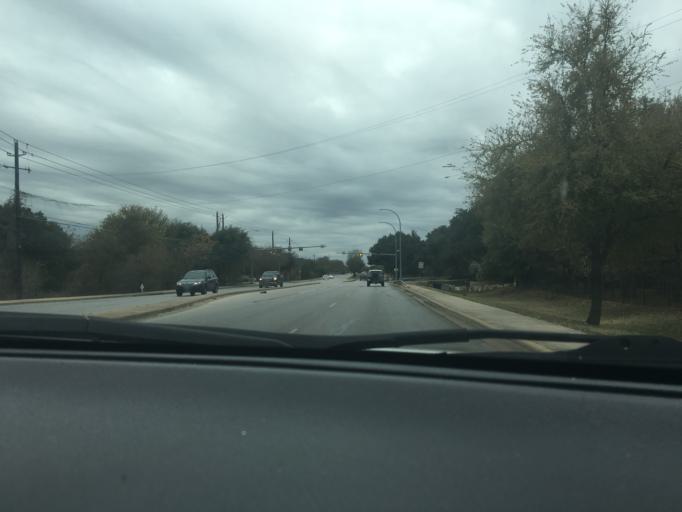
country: US
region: Texas
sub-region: Travis County
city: Rollingwood
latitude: 30.2256
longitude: -97.8231
